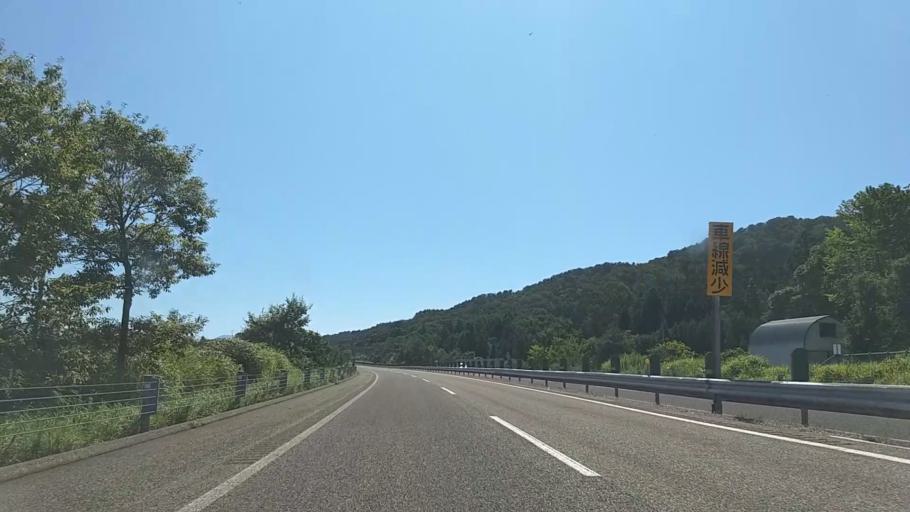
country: JP
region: Niigata
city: Joetsu
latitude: 37.0790
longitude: 138.2243
